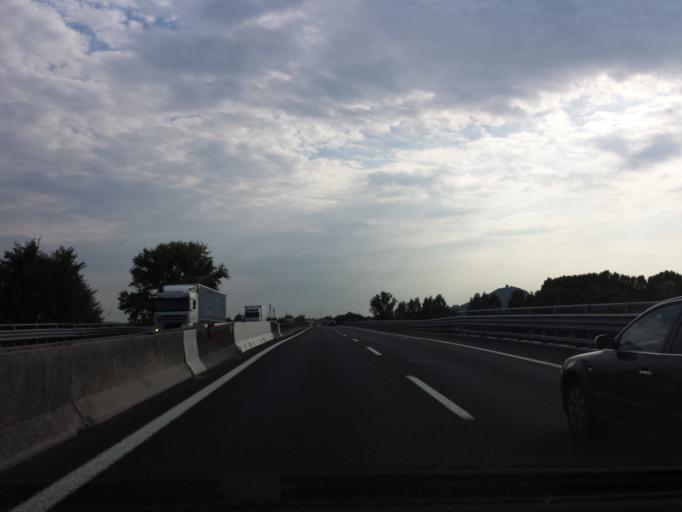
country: IT
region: Veneto
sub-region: Provincia di Padova
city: Pernumia
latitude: 45.2669
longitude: 11.7818
